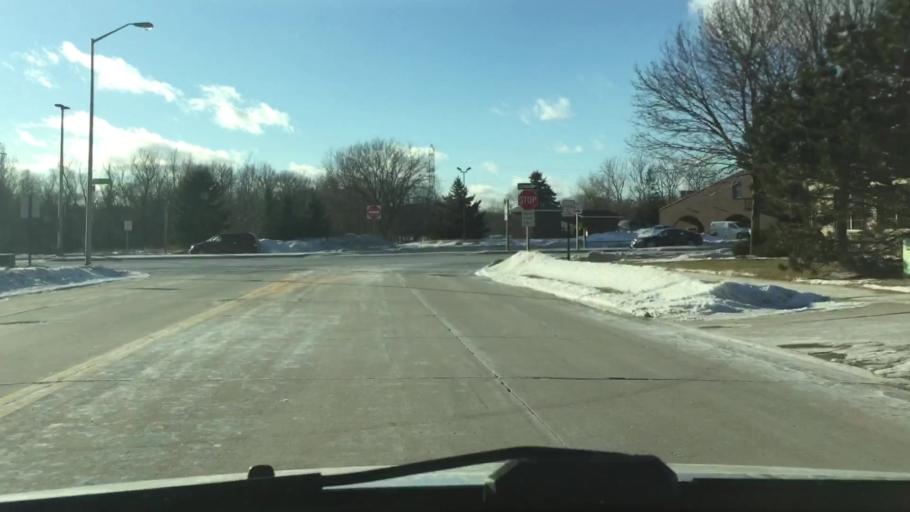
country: US
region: Wisconsin
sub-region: Milwaukee County
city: Hales Corners
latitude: 42.9737
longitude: -88.0469
